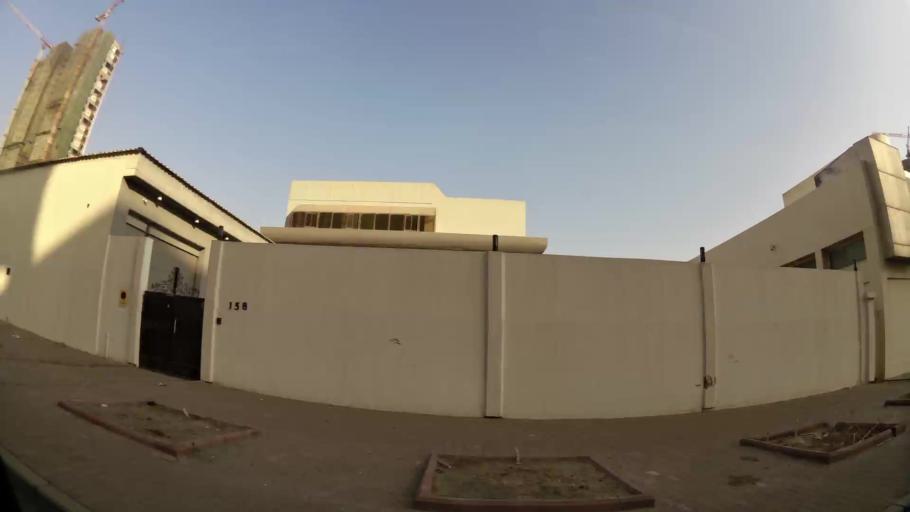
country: KW
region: Muhafazat Hawalli
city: As Salimiyah
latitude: 29.3378
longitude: 48.0605
